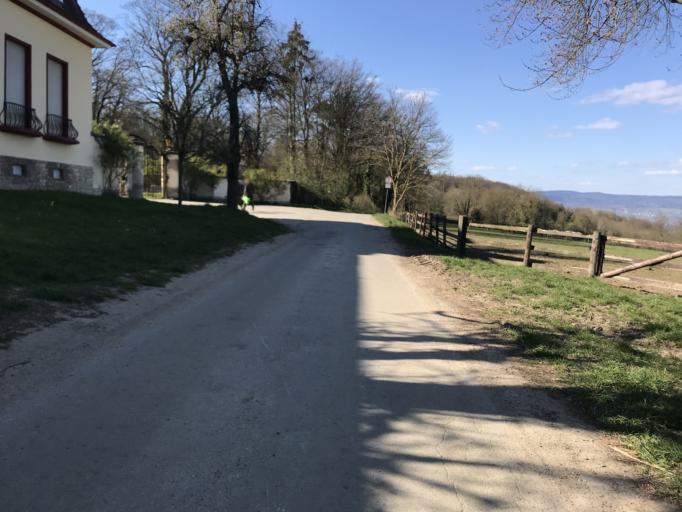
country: DE
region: Rheinland-Pfalz
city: Appenheim
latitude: 49.9418
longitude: 8.0557
